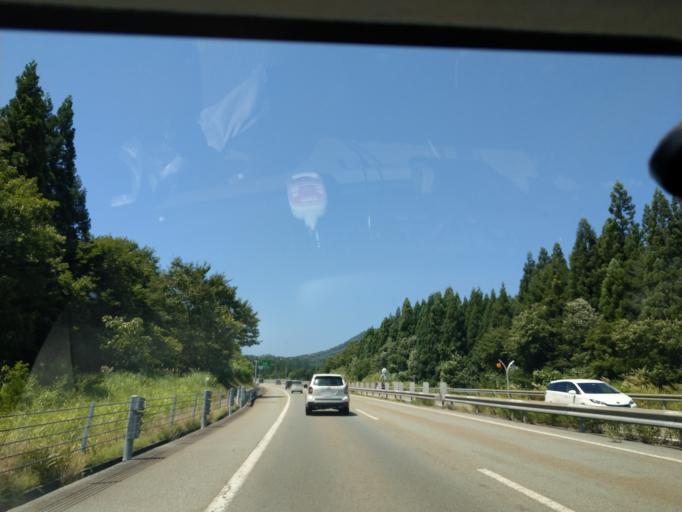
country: JP
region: Akita
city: Omagari
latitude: 39.4245
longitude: 140.4306
